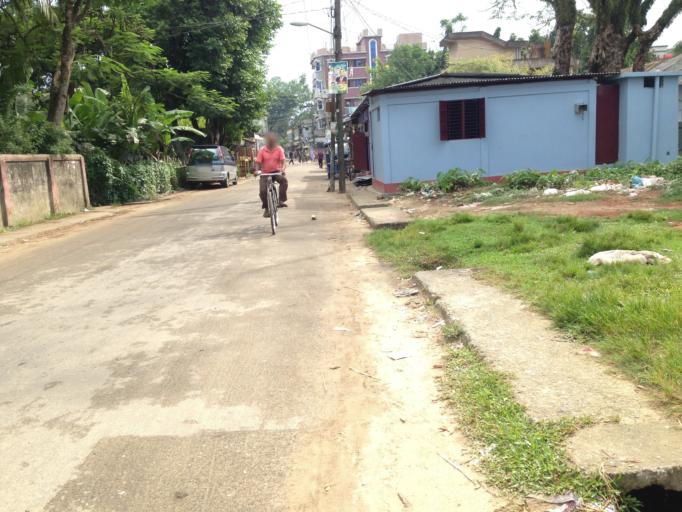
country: IN
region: Tripura
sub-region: Dhalai
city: Kamalpur
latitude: 24.3106
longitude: 91.7276
